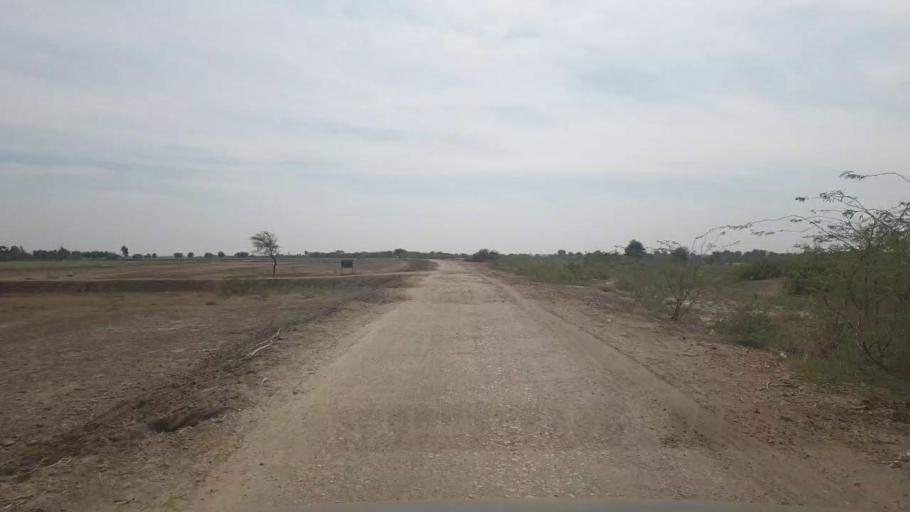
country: PK
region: Sindh
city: Kunri
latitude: 25.2786
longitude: 69.5972
